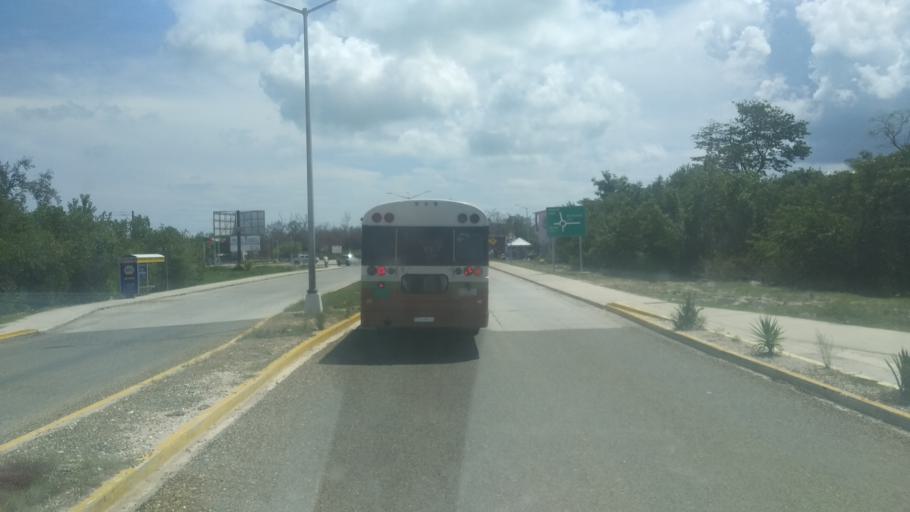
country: BZ
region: Belize
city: Belize City
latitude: 17.5013
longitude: -88.2222
